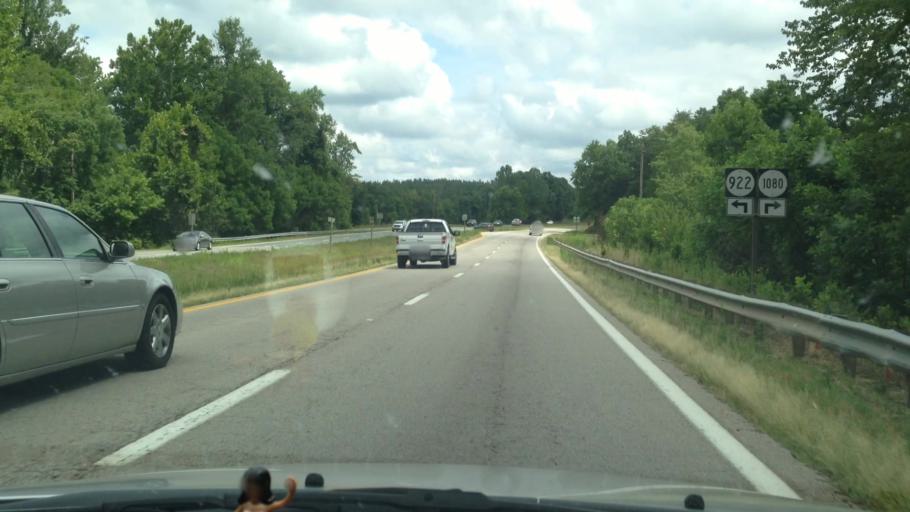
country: US
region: Virginia
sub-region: Pittsylvania County
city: Gretna
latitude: 36.9109
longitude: -79.3877
